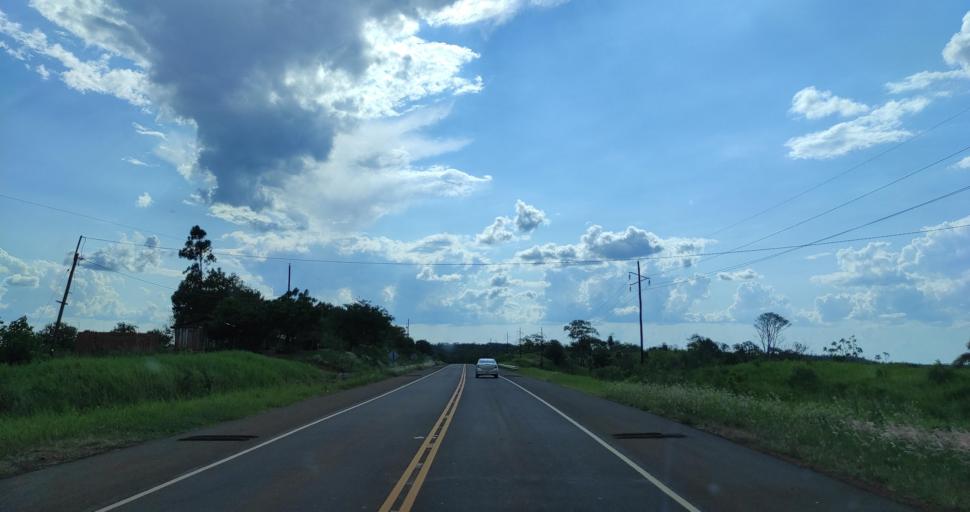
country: AR
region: Misiones
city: Bernardo de Irigoyen
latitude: -26.2985
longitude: -53.8092
